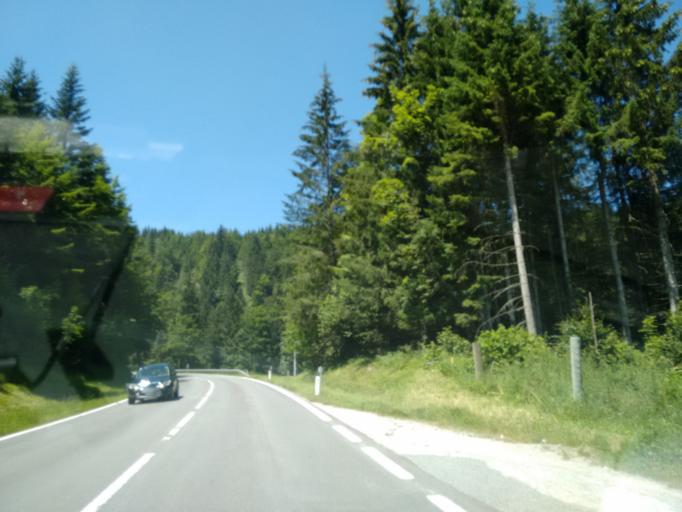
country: AT
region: Styria
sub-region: Politischer Bezirk Liezen
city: Altaussee
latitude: 47.6274
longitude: 13.7081
